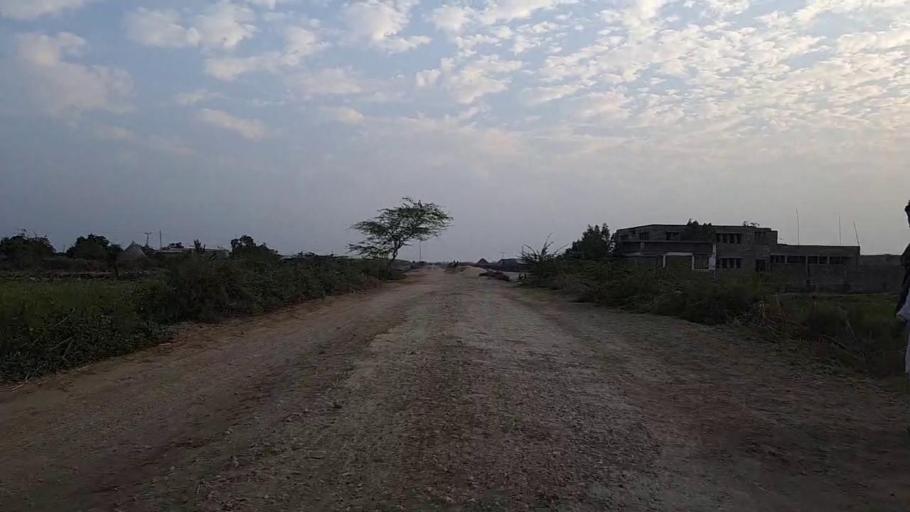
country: PK
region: Sindh
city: Pithoro
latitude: 25.4578
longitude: 69.3455
